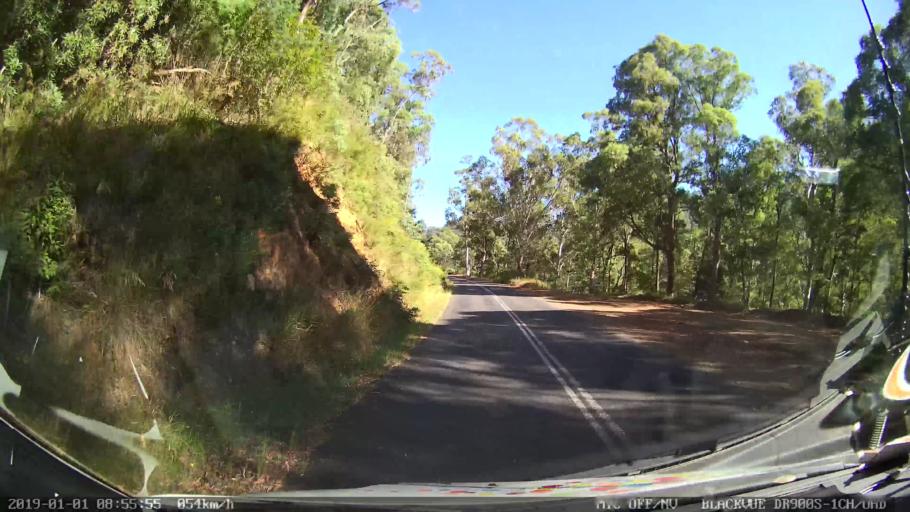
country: AU
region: New South Wales
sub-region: Snowy River
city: Jindabyne
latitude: -36.2503
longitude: 148.1902
